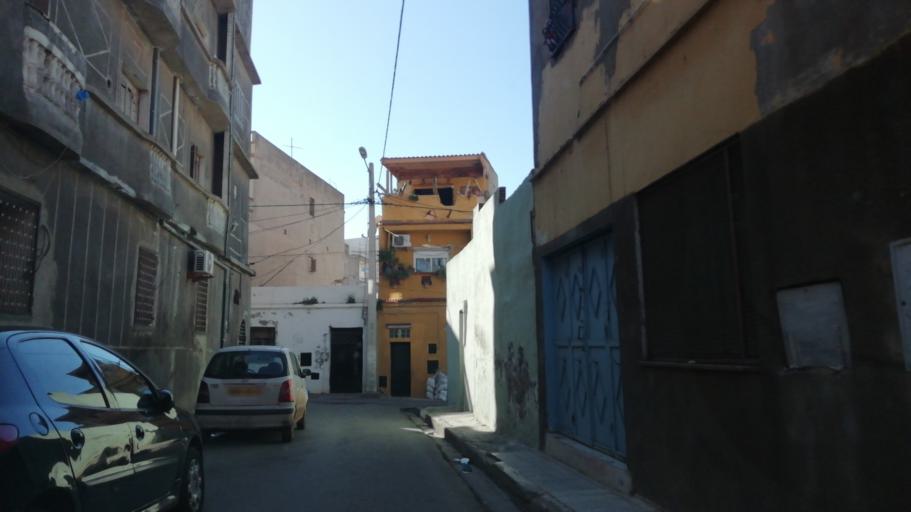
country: DZ
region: Oran
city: Oran
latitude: 35.7055
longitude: -0.6183
